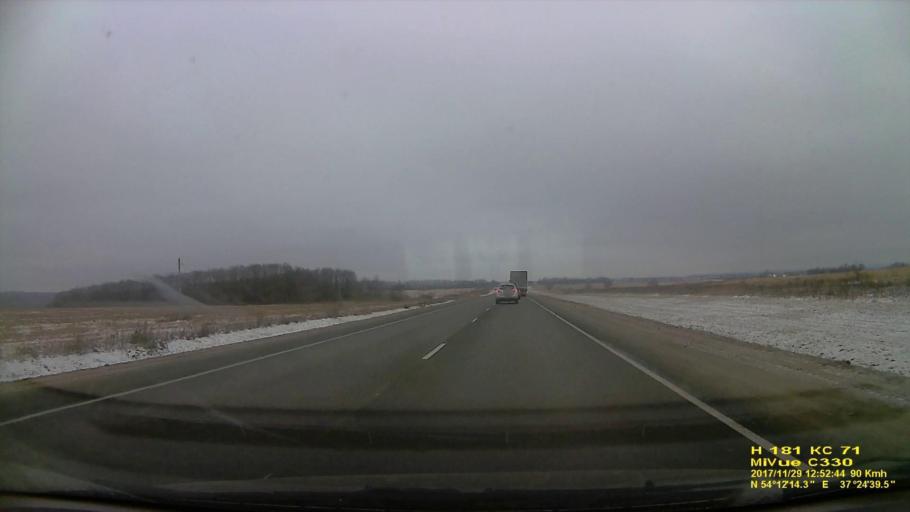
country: RU
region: Tula
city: Leninskiy
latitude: 54.2040
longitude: 37.4109
